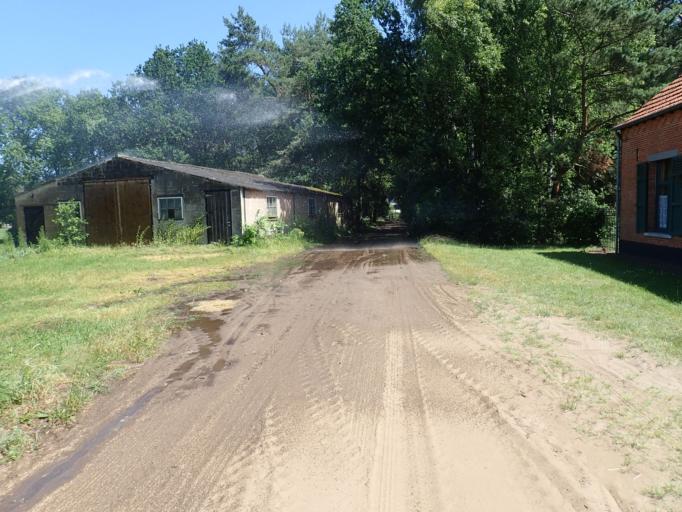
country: BE
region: Flanders
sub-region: Provincie Antwerpen
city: Lille
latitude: 51.2838
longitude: 4.8260
